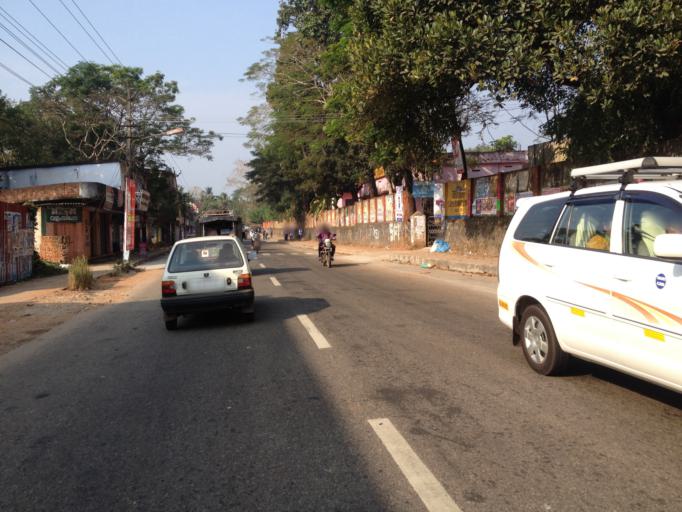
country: IN
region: Kerala
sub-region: Pattanamtitta
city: Adur
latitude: 9.1611
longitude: 76.7200
